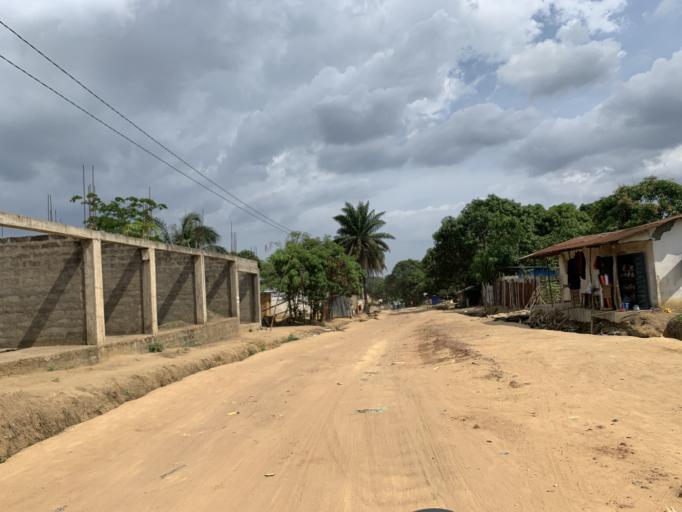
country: SL
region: Western Area
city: Waterloo
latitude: 8.3367
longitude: -13.0528
